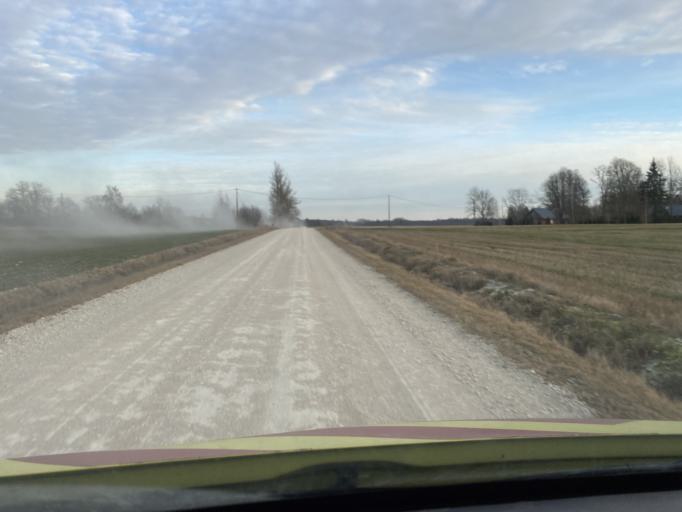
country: EE
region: Jogevamaa
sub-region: Poltsamaa linn
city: Poltsamaa
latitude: 58.5801
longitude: 26.1312
